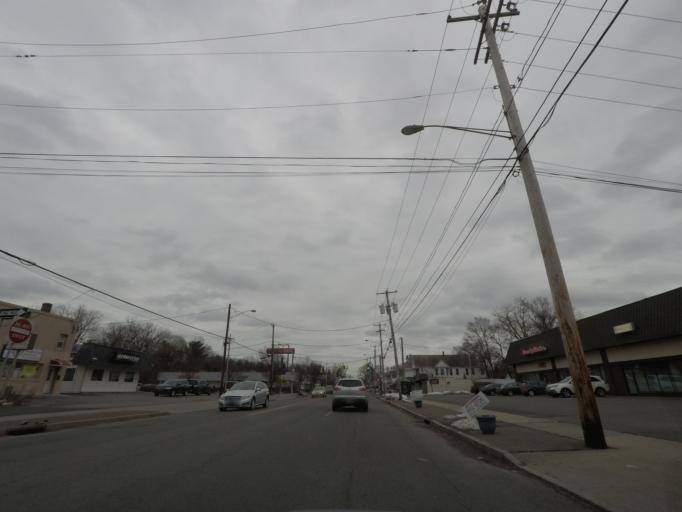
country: US
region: New York
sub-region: Schenectady County
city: Schenectady
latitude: 42.7925
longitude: -73.9177
